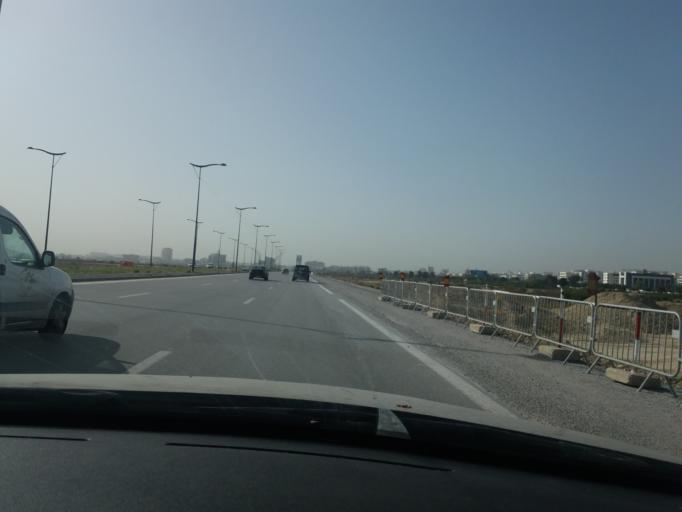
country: TN
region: Tunis
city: Tunis
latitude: 36.8232
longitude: 10.2034
